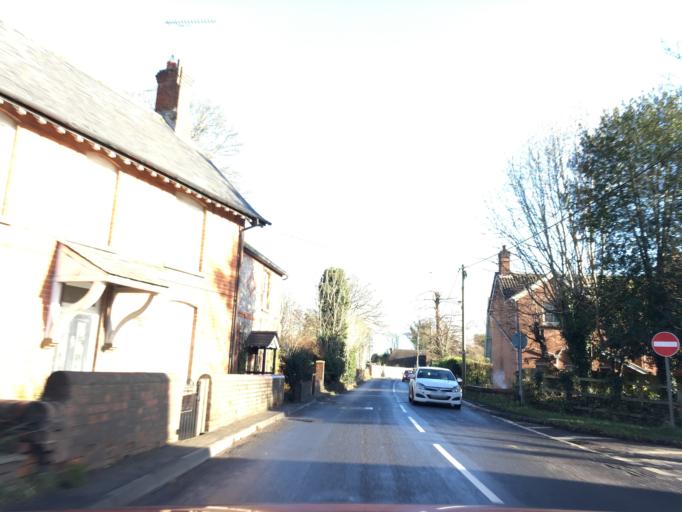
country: GB
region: England
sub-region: Wiltshire
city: Tidworth
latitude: 51.2577
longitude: -1.6248
